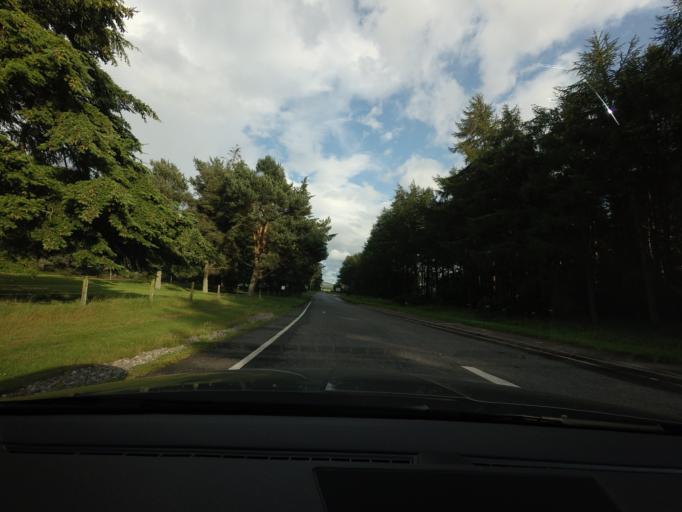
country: GB
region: Scotland
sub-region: Highland
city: Nairn
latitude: 57.5715
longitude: -3.9311
